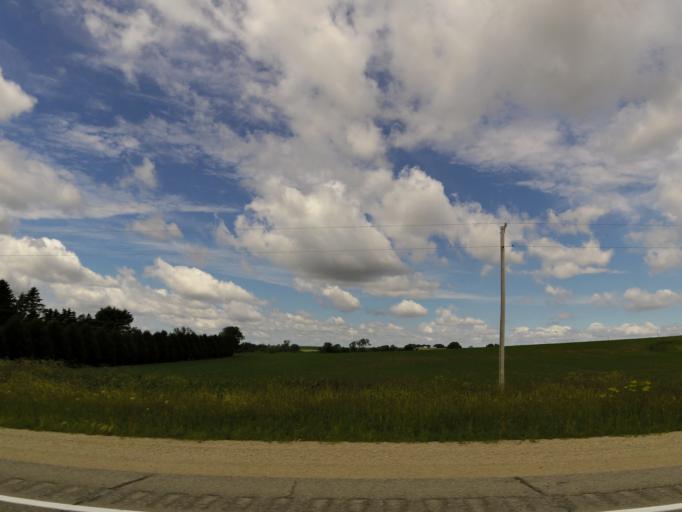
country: US
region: Iowa
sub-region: Chickasaw County
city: New Hampton
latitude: 43.2113
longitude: -92.2984
